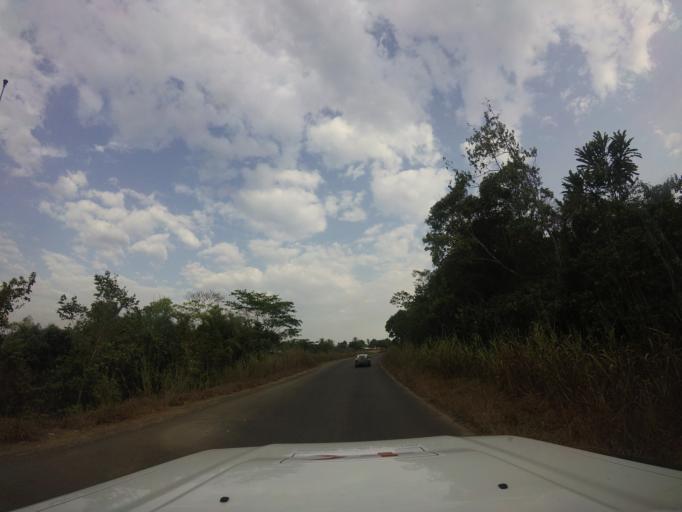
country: LR
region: Grand Cape Mount
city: Robertsport
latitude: 6.9285
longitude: -11.2473
